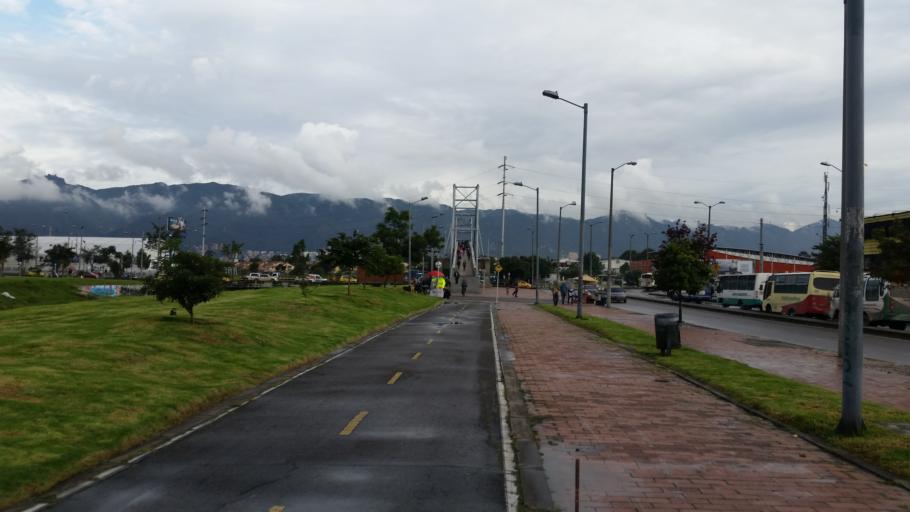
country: CO
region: Bogota D.C.
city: Barrio San Luis
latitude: 4.6864
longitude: -74.0785
